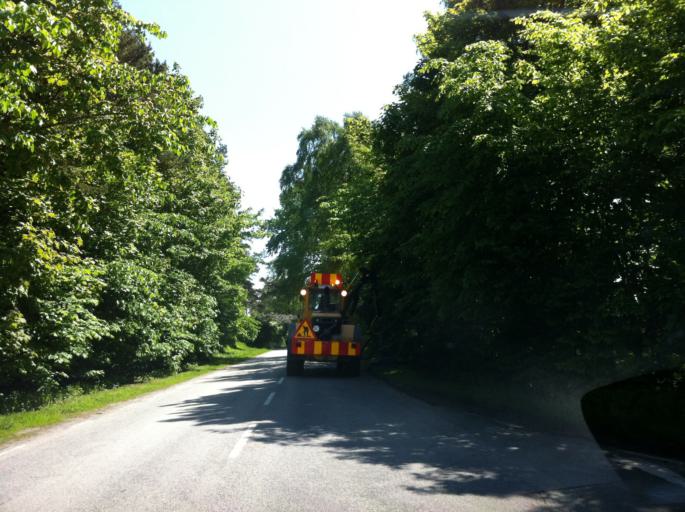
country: SE
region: Skane
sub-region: Kavlinge Kommun
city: Hofterup
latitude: 55.8076
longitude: 12.9818
